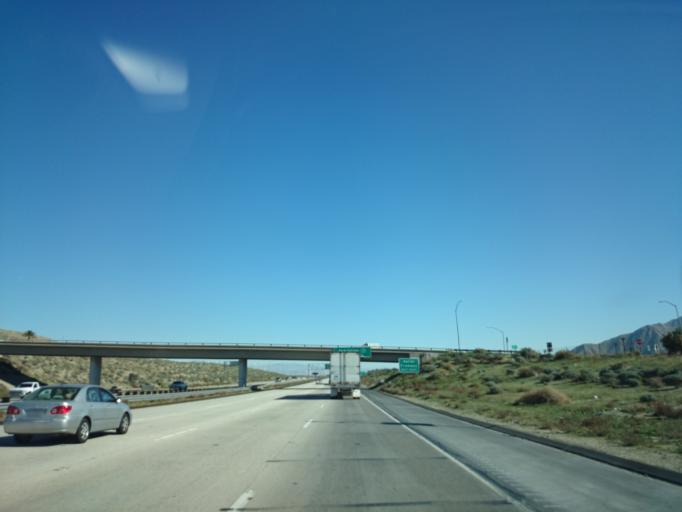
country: US
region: California
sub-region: Riverside County
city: Cabazon
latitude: 33.9238
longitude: -116.6907
